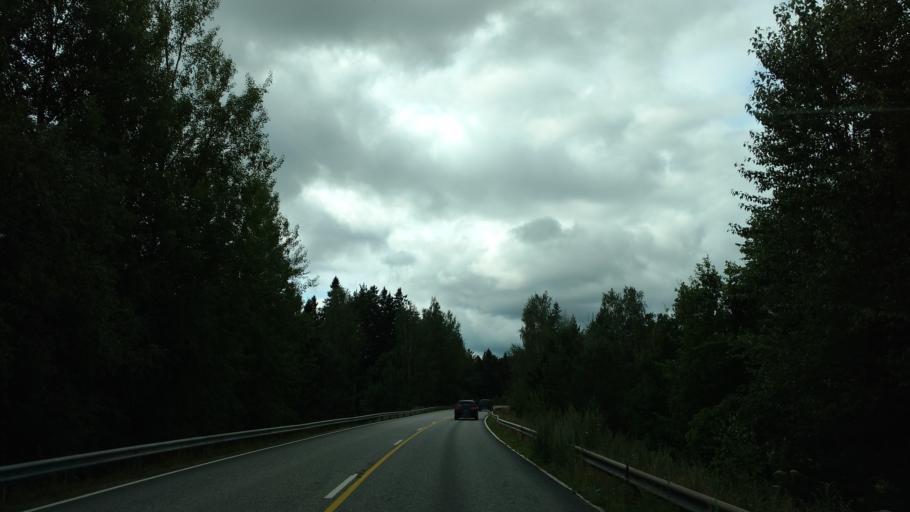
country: FI
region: Varsinais-Suomi
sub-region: Aboland-Turunmaa
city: Kimito
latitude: 60.1409
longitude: 22.6755
